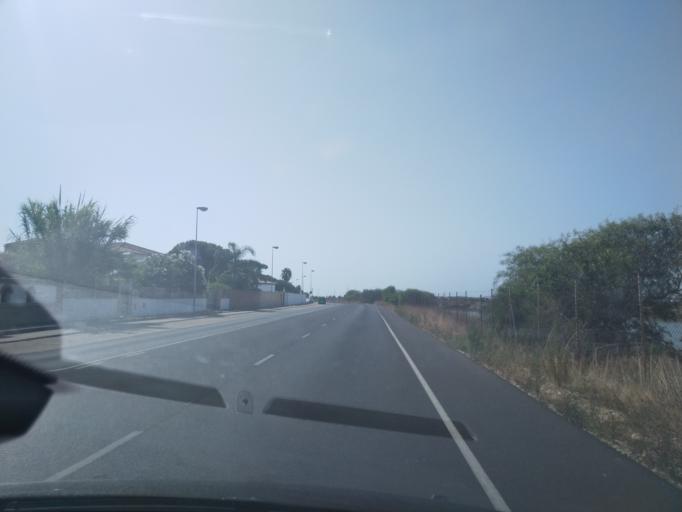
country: ES
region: Andalusia
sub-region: Provincia de Cadiz
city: Chiclana de la Frontera
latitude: 36.3844
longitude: -6.1980
